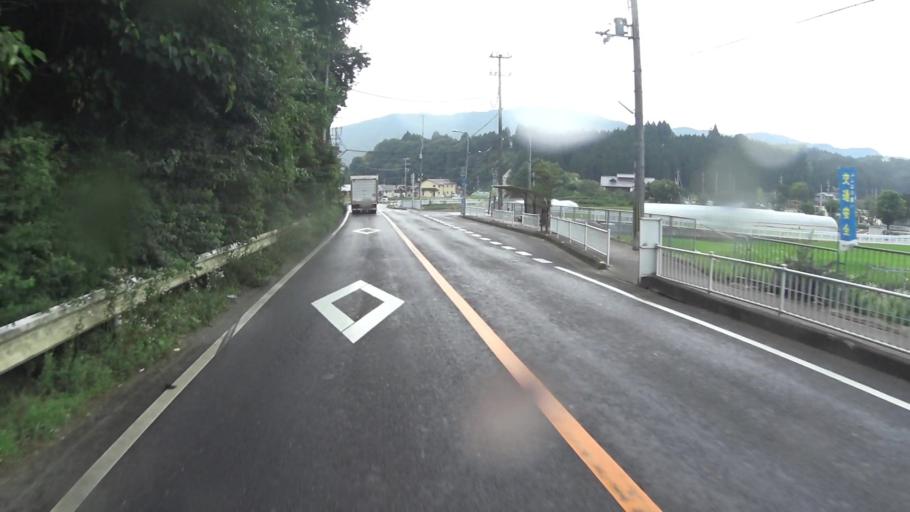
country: JP
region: Kyoto
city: Uji
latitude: 34.8582
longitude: 135.8830
